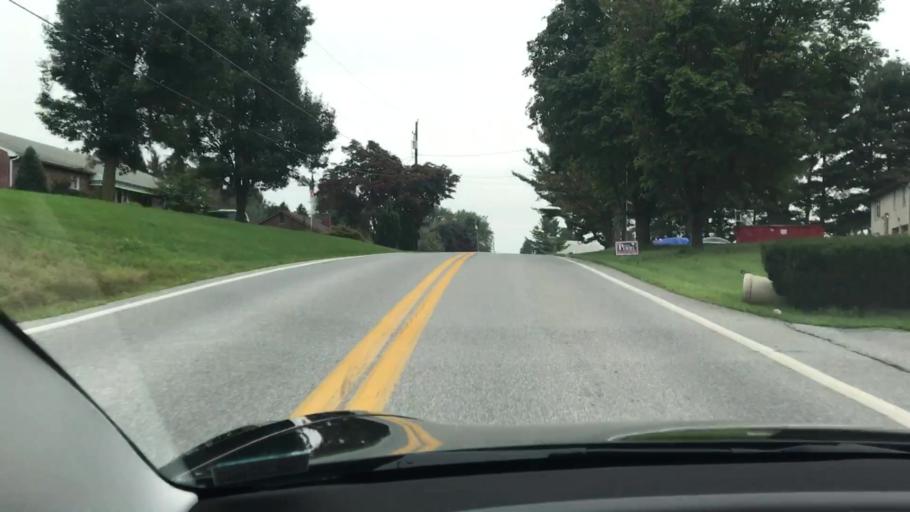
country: US
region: Pennsylvania
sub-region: Cumberland County
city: Lower Allen
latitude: 40.1608
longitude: -76.8890
